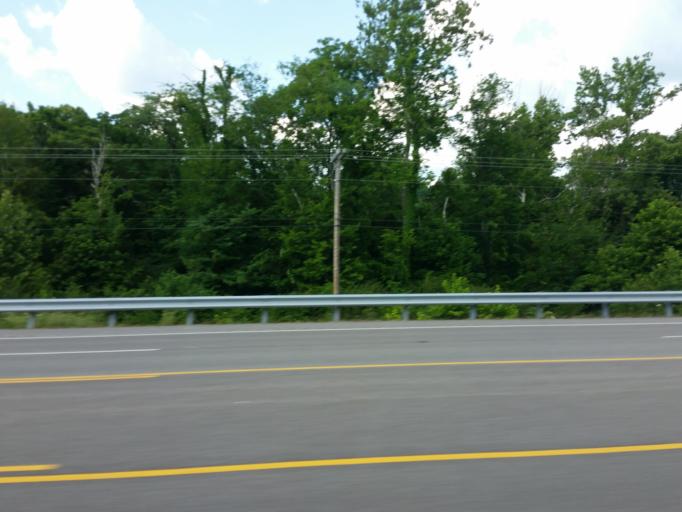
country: US
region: Tennessee
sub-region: Lewis County
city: Hohenwald
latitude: 35.5660
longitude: -87.4027
